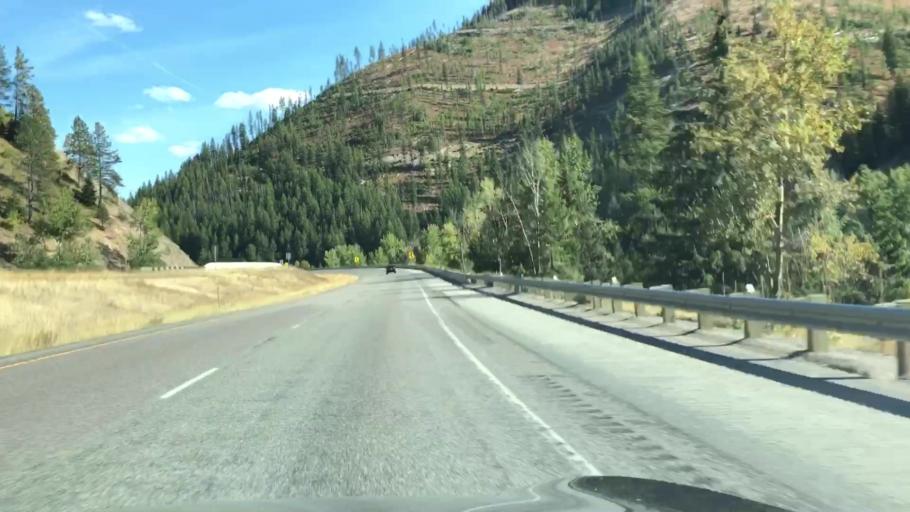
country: US
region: Montana
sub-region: Sanders County
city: Thompson Falls
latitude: 47.4028
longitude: -115.4748
